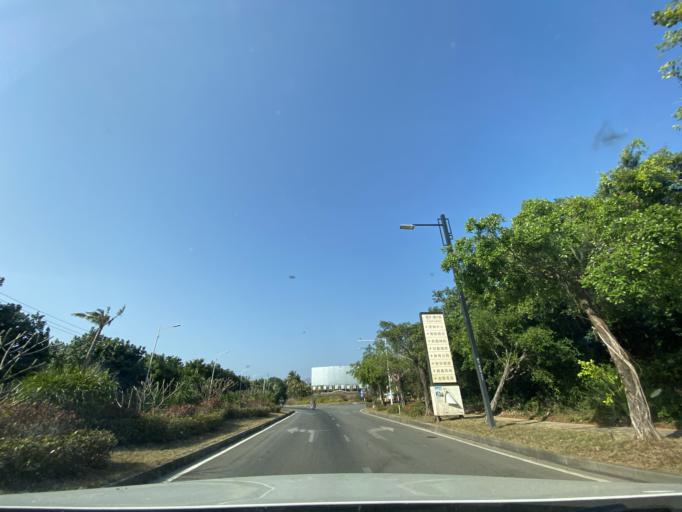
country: CN
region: Hainan
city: Yingzhou
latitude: 18.4460
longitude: 109.8461
